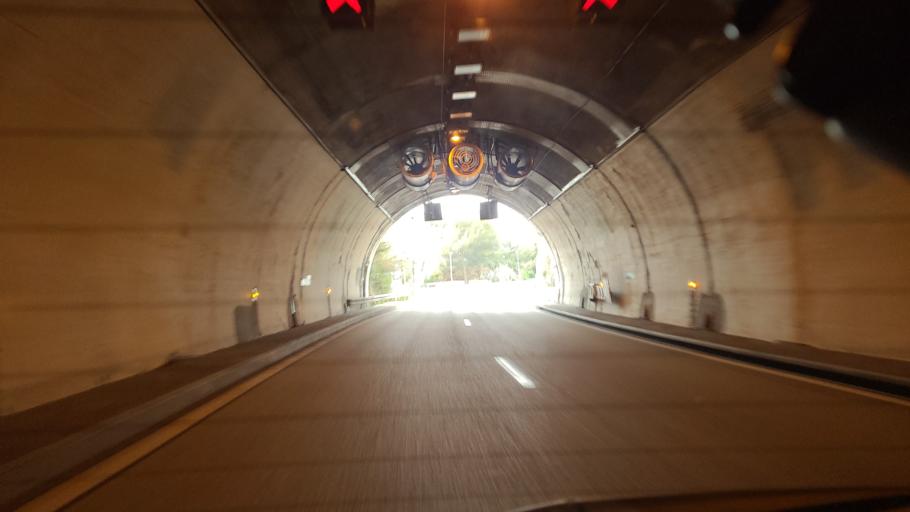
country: FR
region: Provence-Alpes-Cote d'Azur
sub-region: Departement des Alpes-Maritimes
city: Gorbio
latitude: 43.7722
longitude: 7.4501
